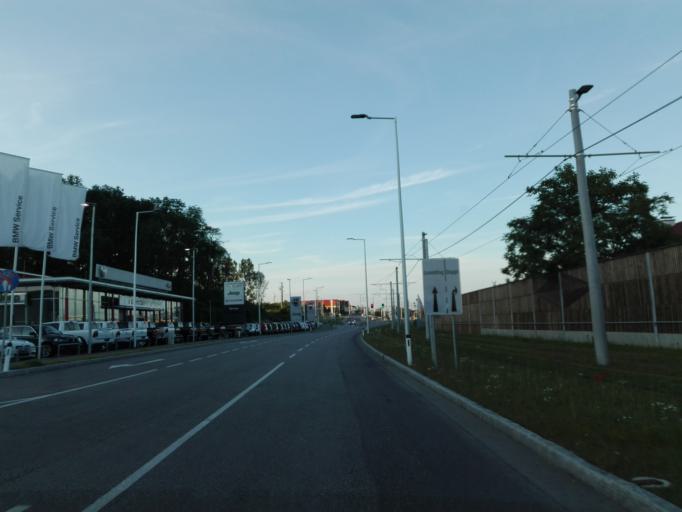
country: AT
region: Upper Austria
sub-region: Politischer Bezirk Linz-Land
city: Traun
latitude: 48.2485
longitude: 14.2418
